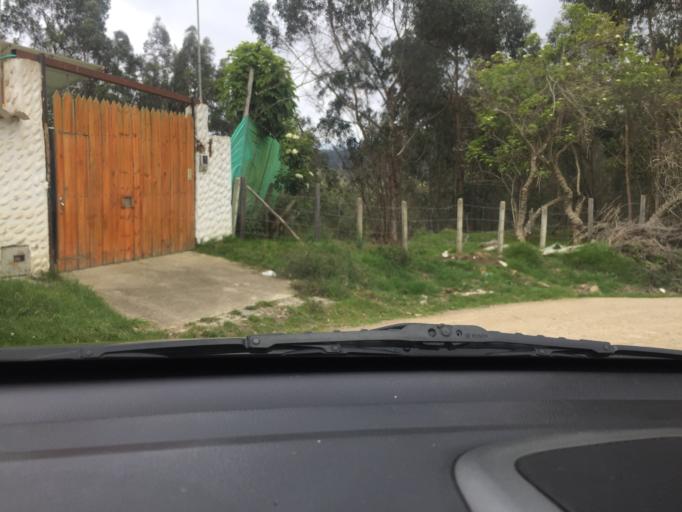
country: CO
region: Cundinamarca
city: Zipacon
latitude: 4.7622
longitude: -74.3777
